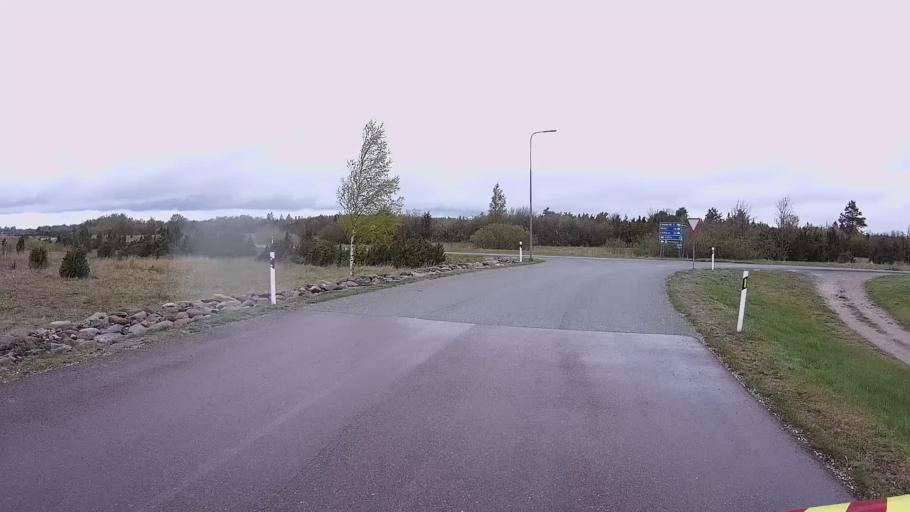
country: EE
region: Hiiumaa
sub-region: Kaerdla linn
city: Kardla
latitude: 58.6944
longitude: 22.5216
